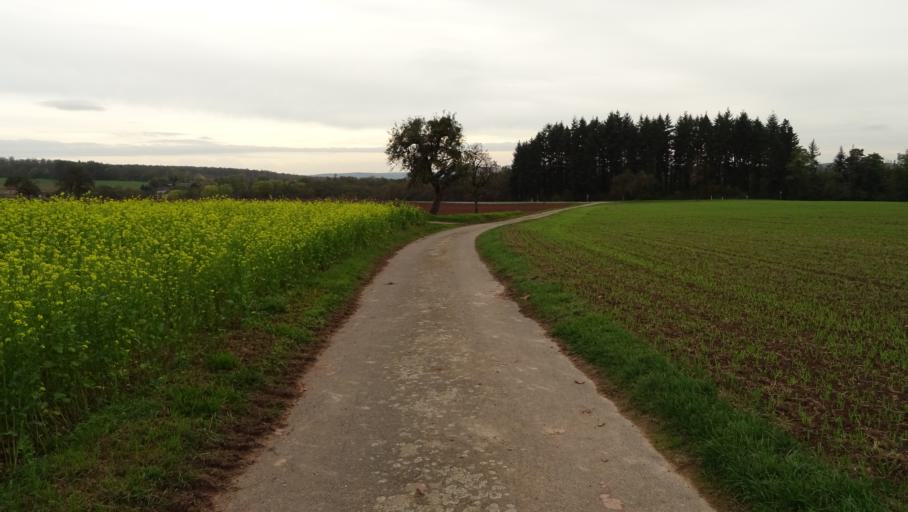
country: DE
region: Baden-Wuerttemberg
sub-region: Karlsruhe Region
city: Neckargerach
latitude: 49.3939
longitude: 9.0857
